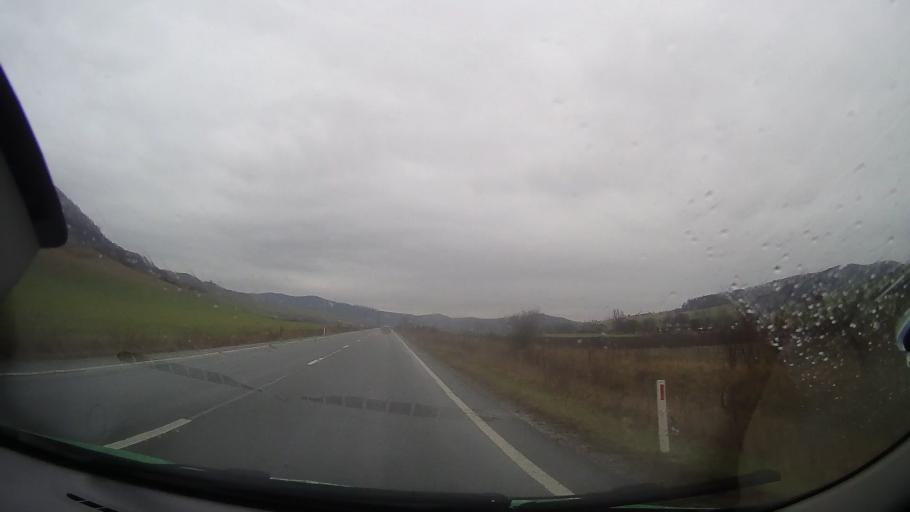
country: RO
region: Bistrita-Nasaud
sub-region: Comuna Teaca
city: Teaca
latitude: 46.9324
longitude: 24.4804
